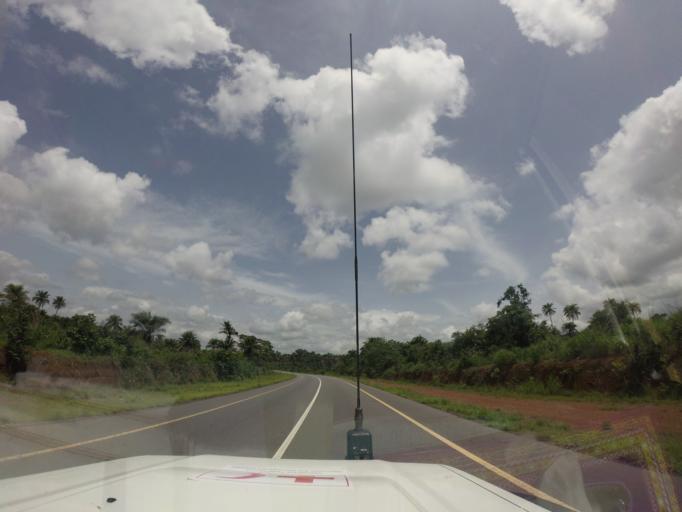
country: SL
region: Northern Province
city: Mange
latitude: 8.8947
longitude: -12.8388
